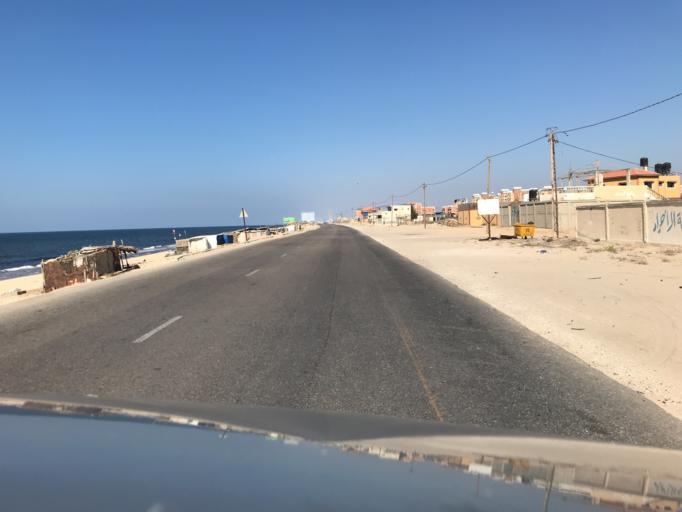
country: PS
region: Gaza Strip
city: An Nusayrat
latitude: 31.4669
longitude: 34.3793
